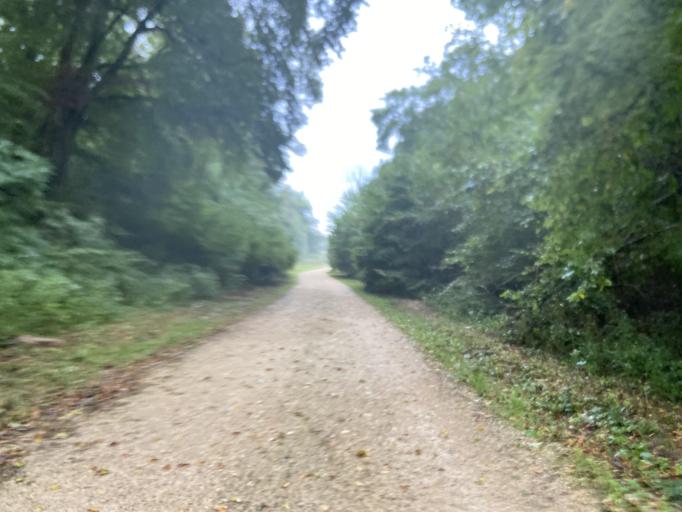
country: DE
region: Baden-Wuerttemberg
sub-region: Tuebingen Region
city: Bingen
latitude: 48.1250
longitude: 9.2592
